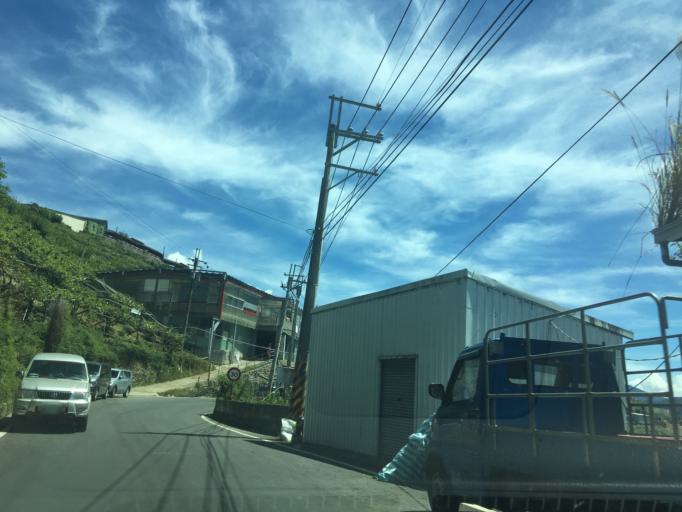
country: TW
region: Taiwan
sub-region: Nantou
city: Puli
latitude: 24.2530
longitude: 121.2598
